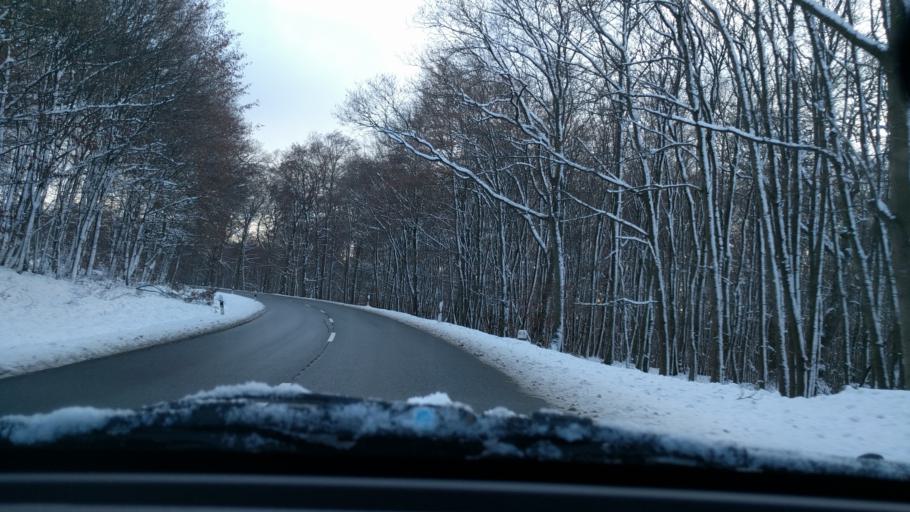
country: DE
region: Hesse
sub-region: Regierungsbezirk Darmstadt
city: Walluf
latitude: 50.0935
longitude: 8.1460
